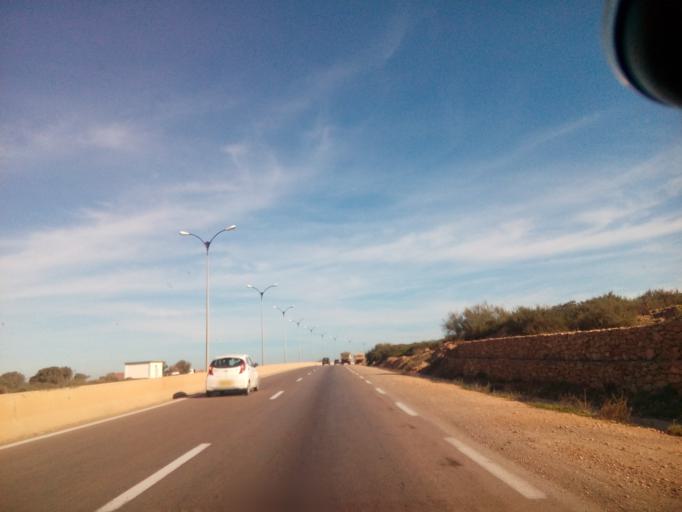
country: DZ
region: Oran
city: Ain el Bya
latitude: 35.7932
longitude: -0.0926
